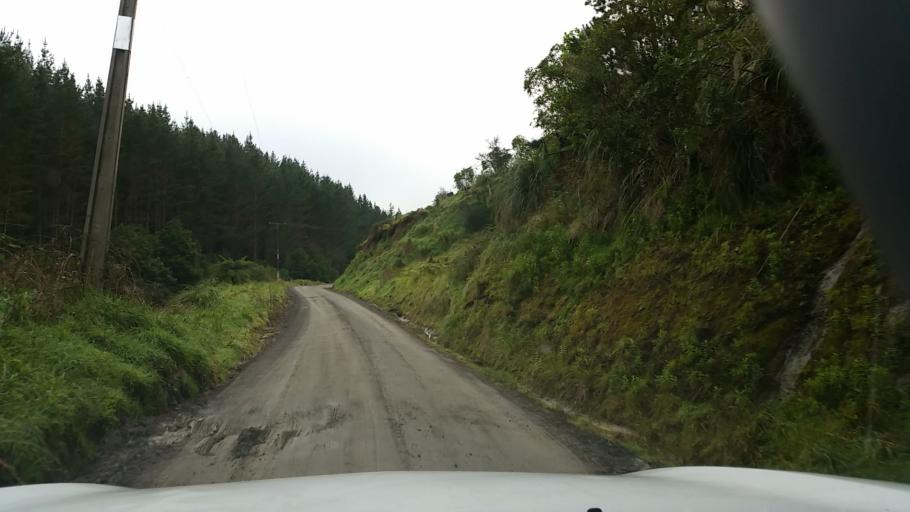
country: NZ
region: Taranaki
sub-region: South Taranaki District
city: Hawera
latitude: -39.5257
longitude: 174.4094
